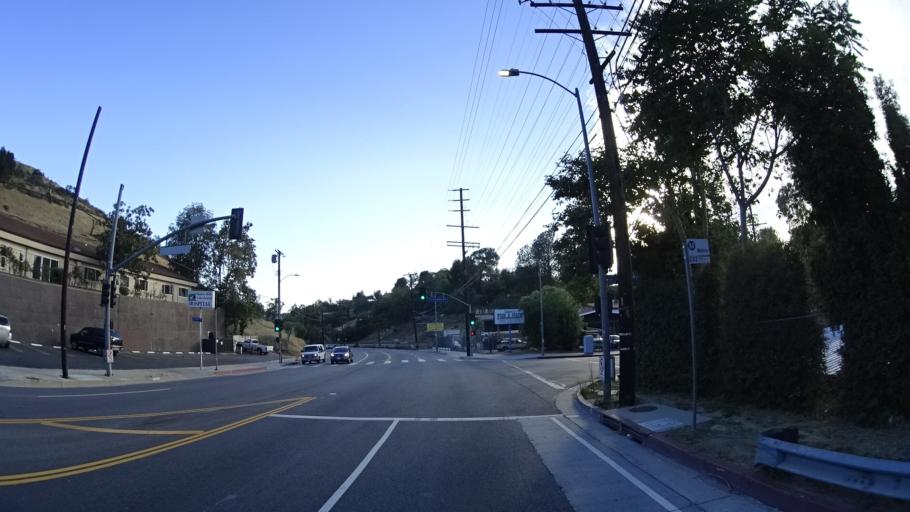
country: US
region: California
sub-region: Los Angeles County
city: Burbank
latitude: 34.2604
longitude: -118.3391
